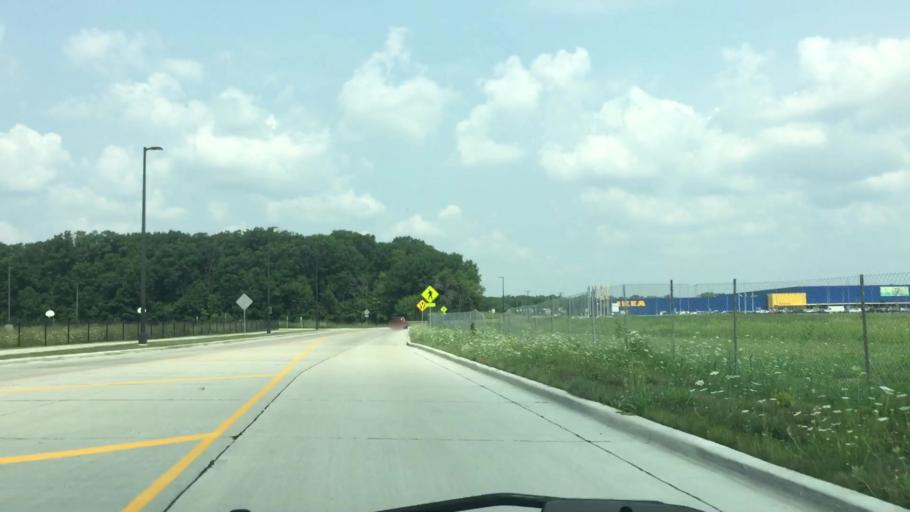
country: US
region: Wisconsin
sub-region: Milwaukee County
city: Greendale
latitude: 42.9031
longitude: -87.9413
